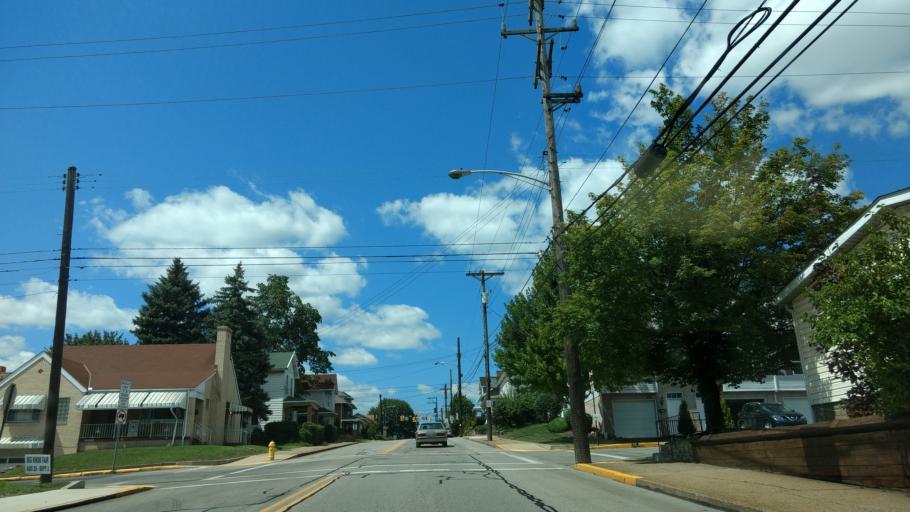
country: US
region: Pennsylvania
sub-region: Beaver County
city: Rochester
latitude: 40.7054
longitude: -80.2784
